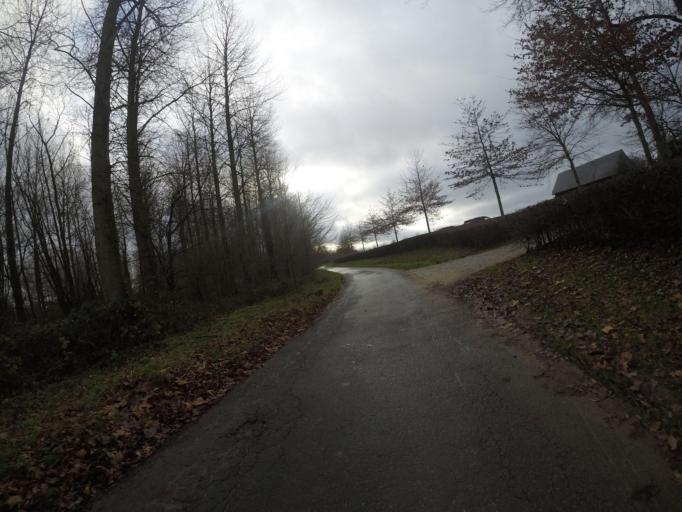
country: BE
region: Flanders
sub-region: Provincie Vlaams-Brabant
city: Gooik
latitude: 50.8060
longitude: 4.1247
